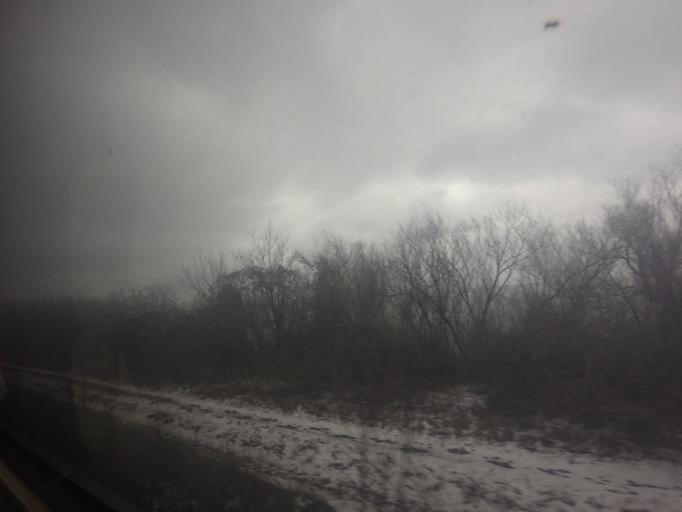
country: CA
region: Ontario
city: Cobourg
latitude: 43.9409
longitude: -78.3038
